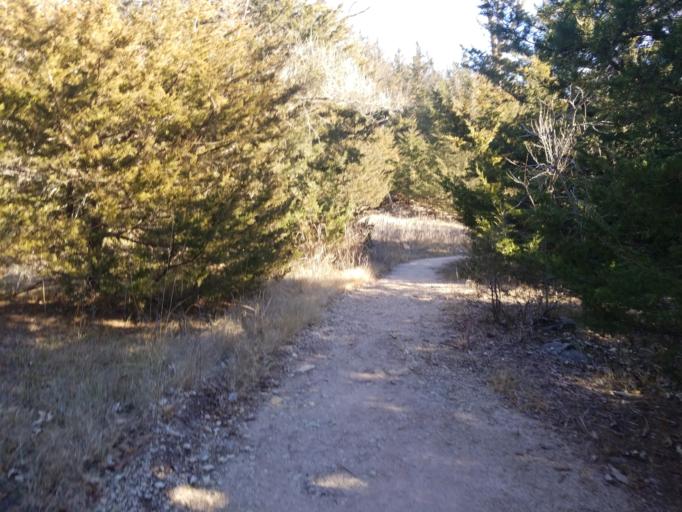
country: US
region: Nebraska
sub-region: Saunders County
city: Ashland
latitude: 41.0151
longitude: -96.2893
